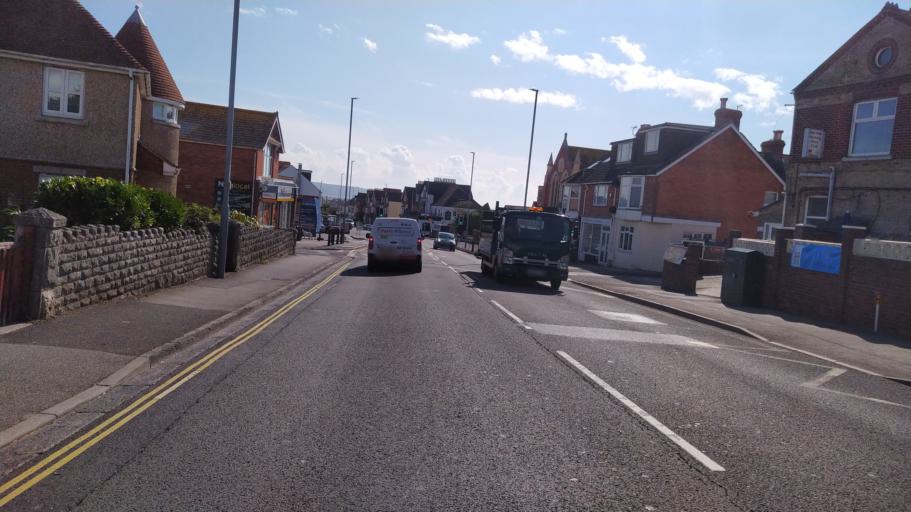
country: GB
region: England
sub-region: Dorset
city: Weymouth
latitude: 50.5953
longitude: -2.4756
